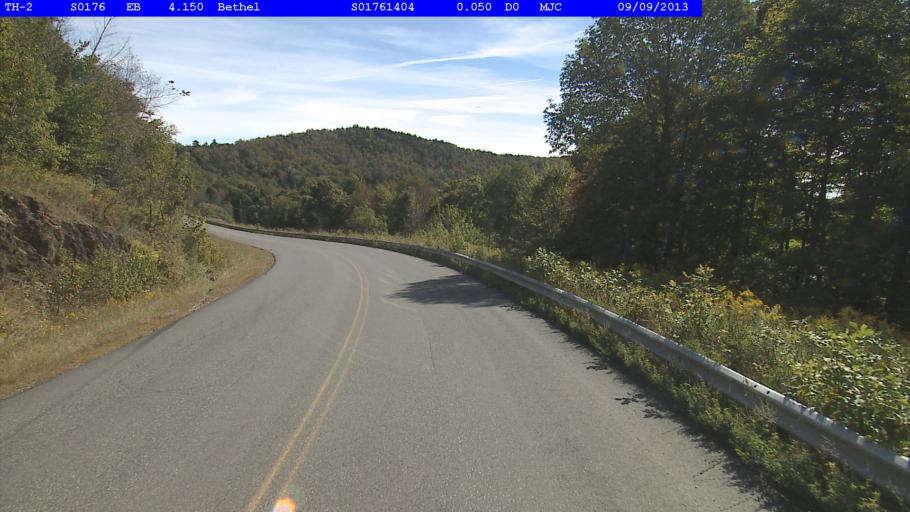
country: US
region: Vermont
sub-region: Orange County
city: Randolph
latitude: 43.8491
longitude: -72.7491
